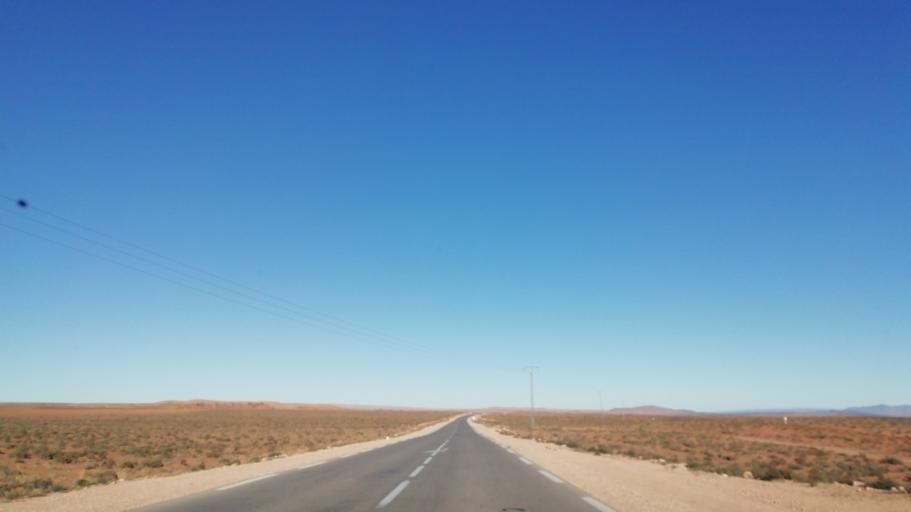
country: DZ
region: El Bayadh
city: El Abiodh Sidi Cheikh
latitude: 33.1296
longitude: 0.2871
